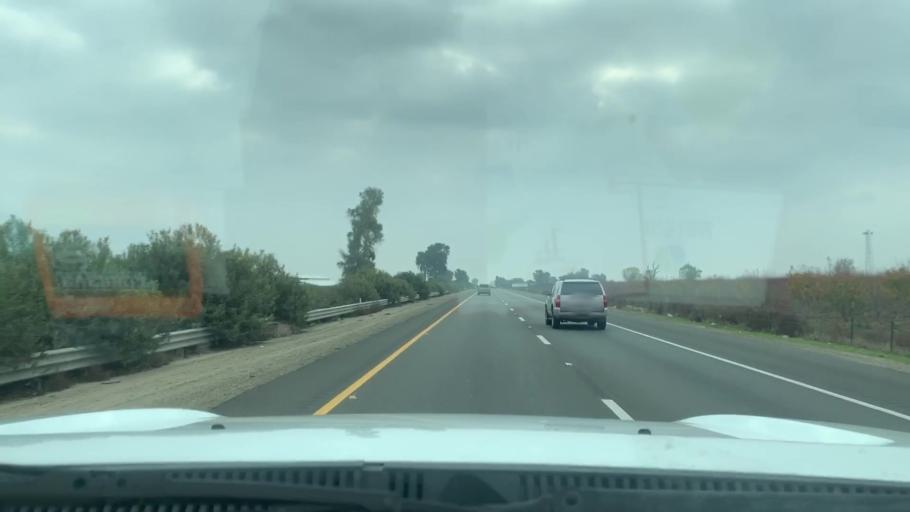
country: US
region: California
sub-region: Tulare County
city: Tipton
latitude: 36.1168
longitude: -119.3243
